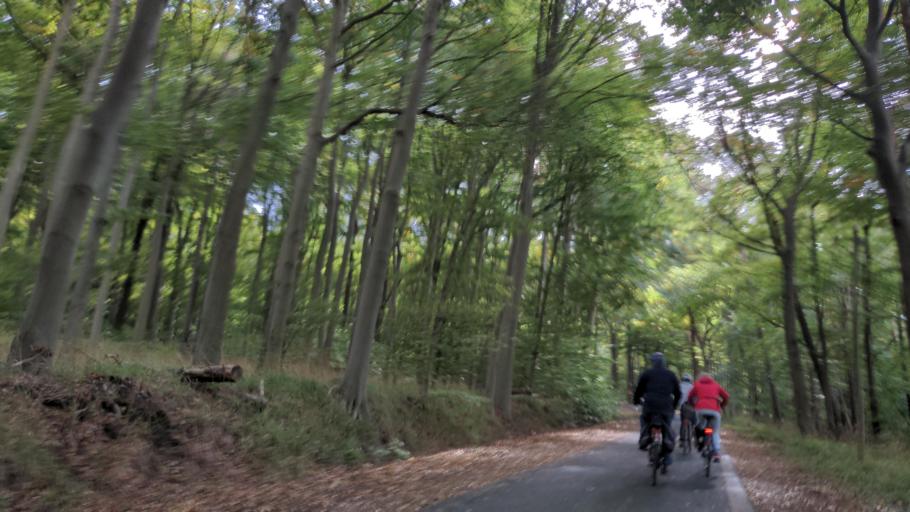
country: DE
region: Schleswig-Holstein
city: Buchholz
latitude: 53.7395
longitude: 10.7653
